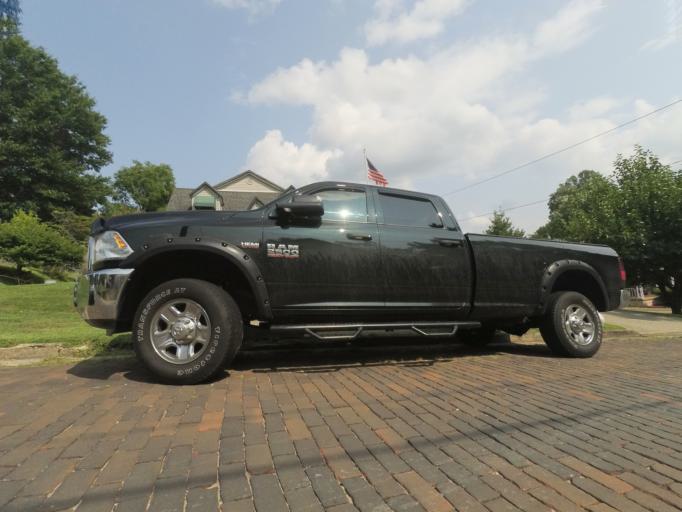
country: US
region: West Virginia
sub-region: Cabell County
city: Huntington
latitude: 38.4022
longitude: -82.4041
